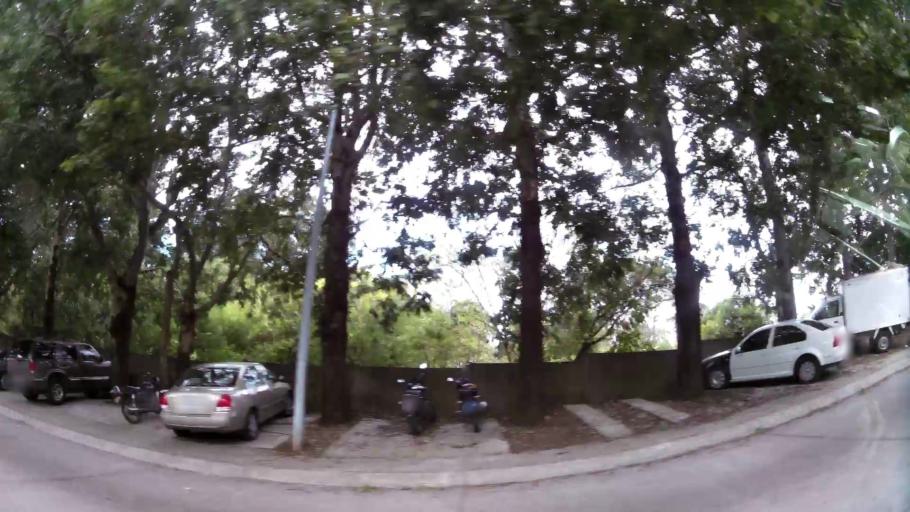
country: GT
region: Guatemala
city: Santa Catarina Pinula
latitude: 14.5714
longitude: -90.5352
